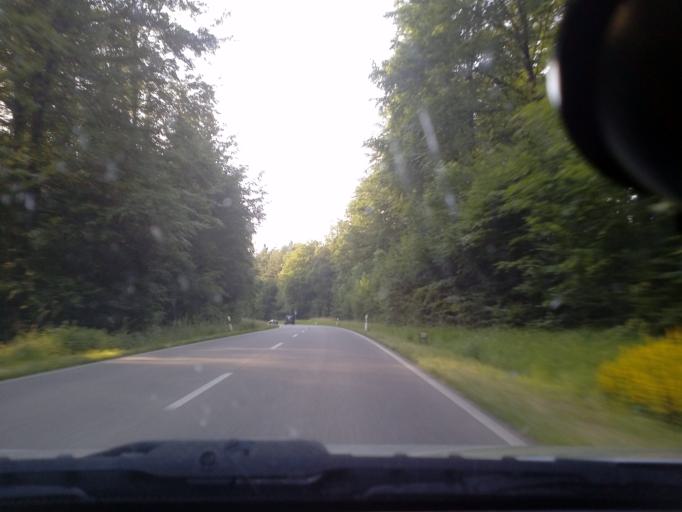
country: DE
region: Baden-Wuerttemberg
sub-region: Karlsruhe Region
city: Woessingen
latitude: 48.9932
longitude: 8.6356
